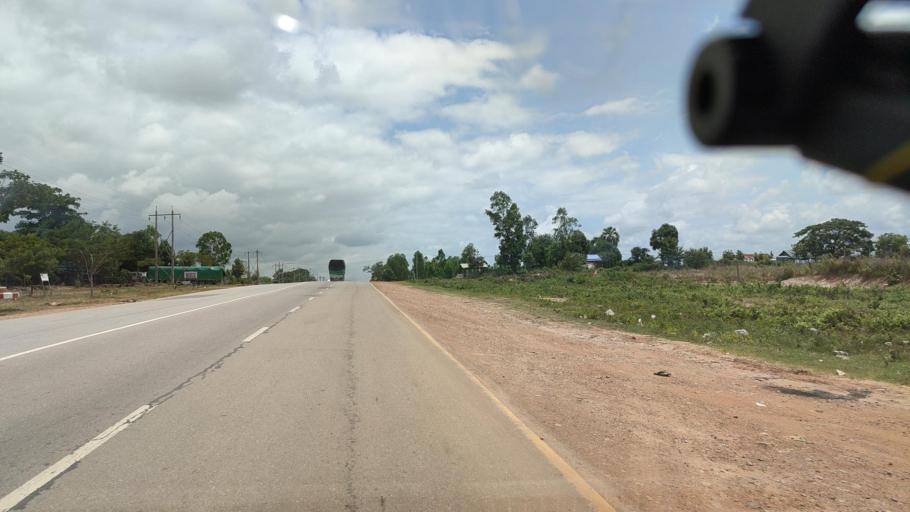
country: MM
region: Mandalay
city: Pyinmana
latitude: 19.5624
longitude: 96.2466
